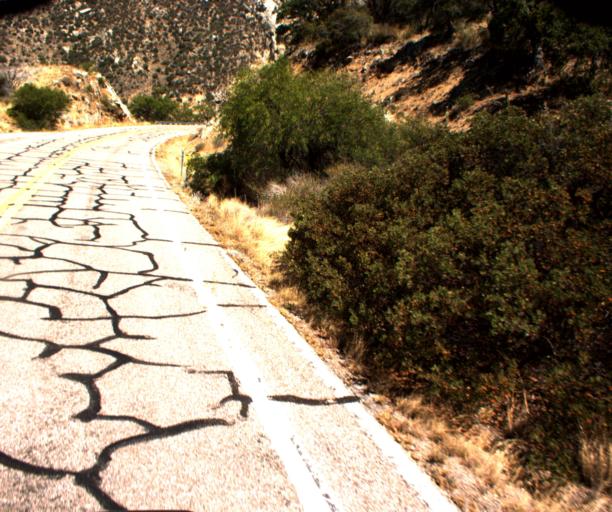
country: US
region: Arizona
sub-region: Pima County
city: Sells
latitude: 31.9726
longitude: -111.6164
